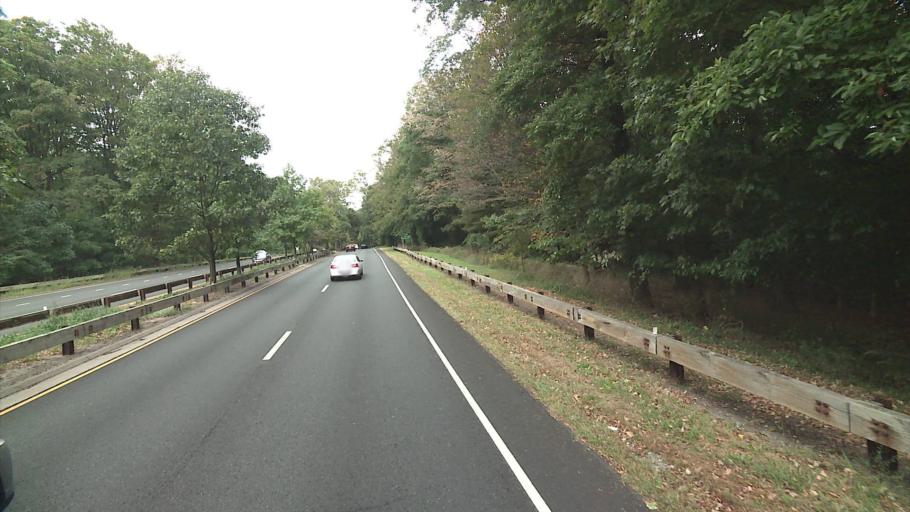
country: US
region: Connecticut
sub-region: Fairfield County
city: Glenville
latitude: 41.0913
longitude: -73.6283
